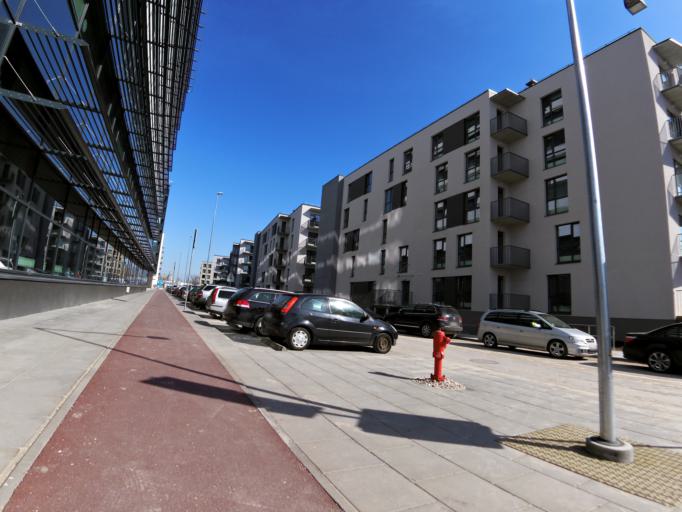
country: LT
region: Vilnius County
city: Seskine
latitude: 54.7209
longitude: 25.2798
